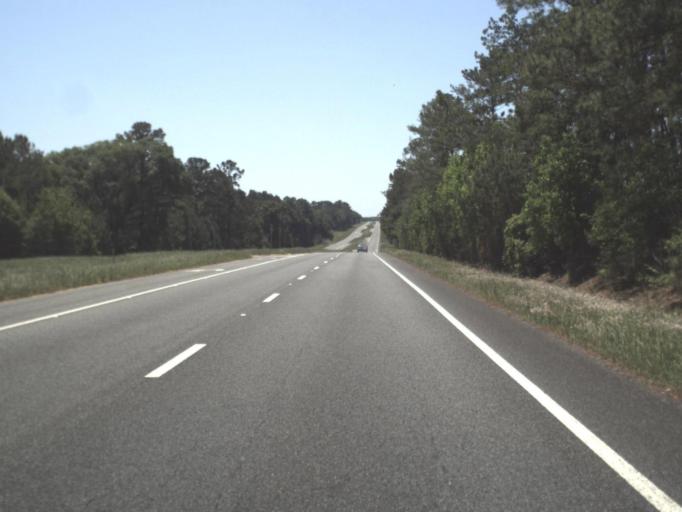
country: US
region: Florida
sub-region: Jefferson County
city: Monticello
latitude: 30.6594
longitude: -83.8780
